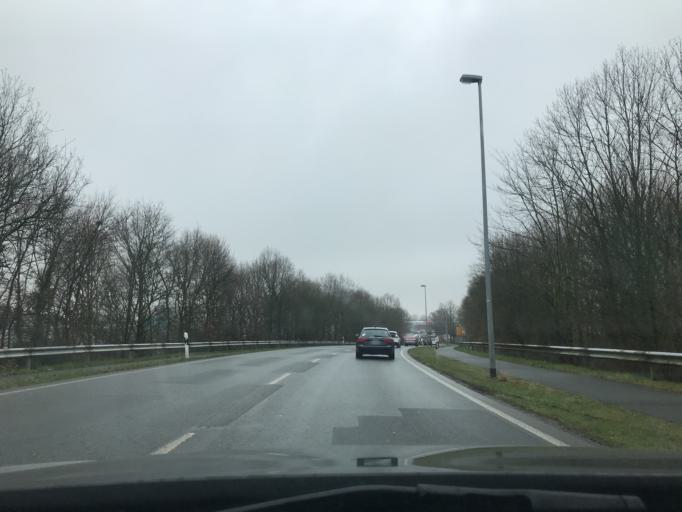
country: DE
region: North Rhine-Westphalia
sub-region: Regierungsbezirk Dusseldorf
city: Kleve
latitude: 51.7978
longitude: 6.1344
